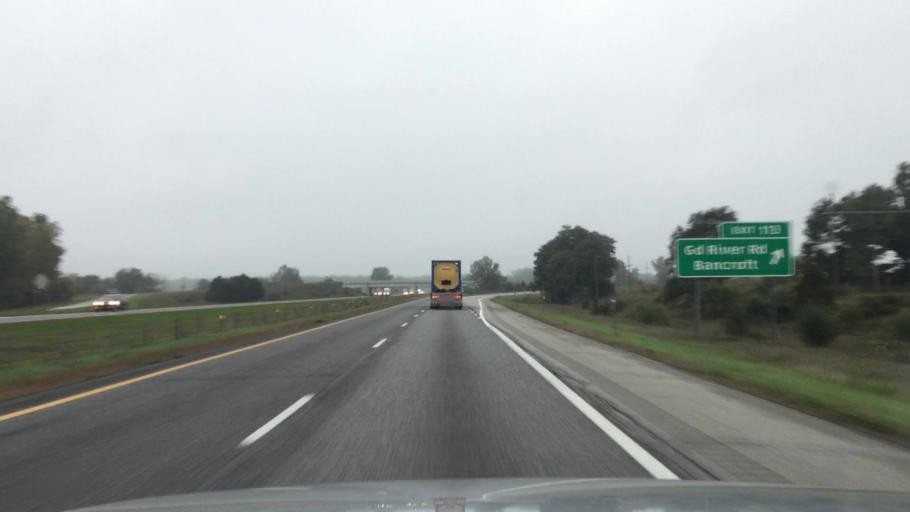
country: US
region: Michigan
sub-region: Shiawassee County
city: Corunna
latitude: 42.8970
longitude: -84.0871
